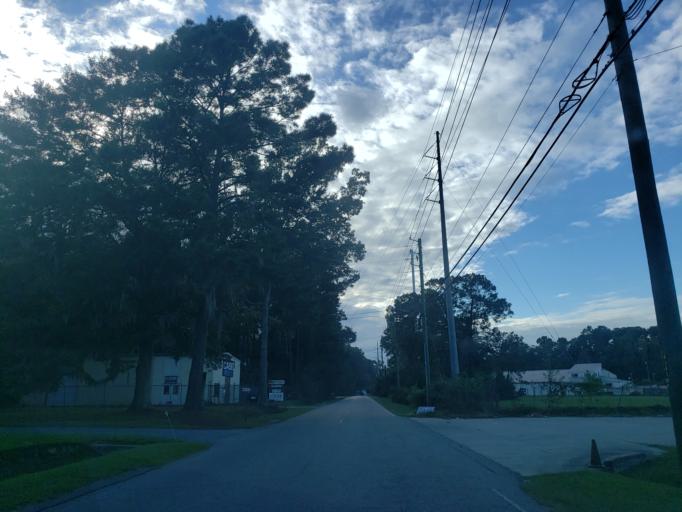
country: US
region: Georgia
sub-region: Chatham County
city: Georgetown
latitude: 31.9903
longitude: -81.2291
